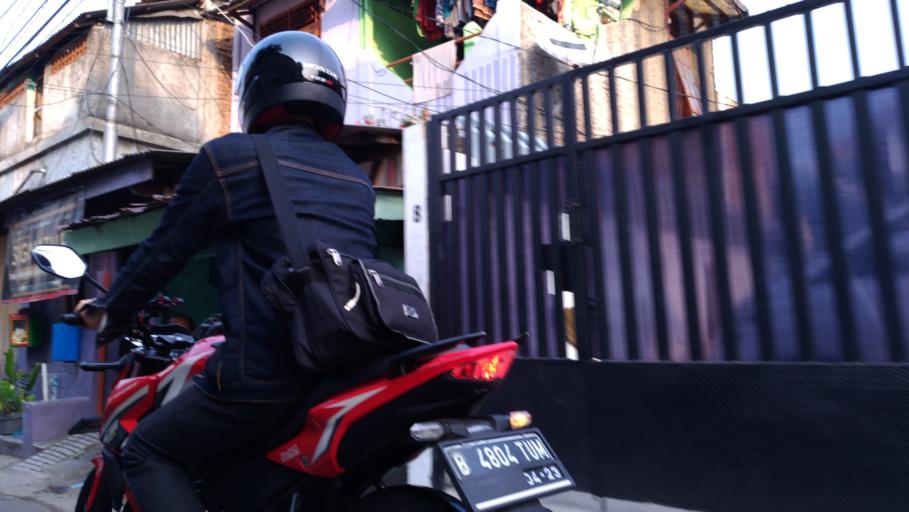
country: ID
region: Jakarta Raya
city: Jakarta
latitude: -6.2197
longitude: 106.8666
